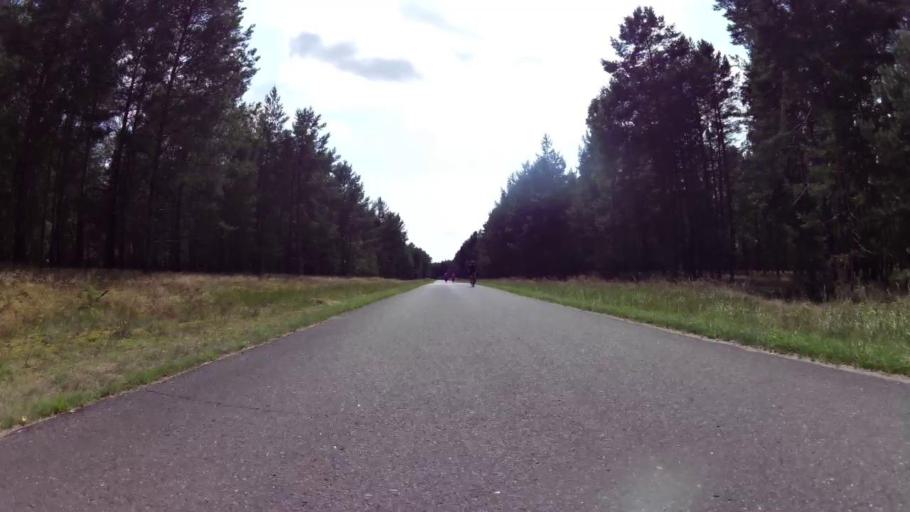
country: PL
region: West Pomeranian Voivodeship
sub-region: Powiat choszczenski
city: Drawno
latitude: 53.3617
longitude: 15.7082
